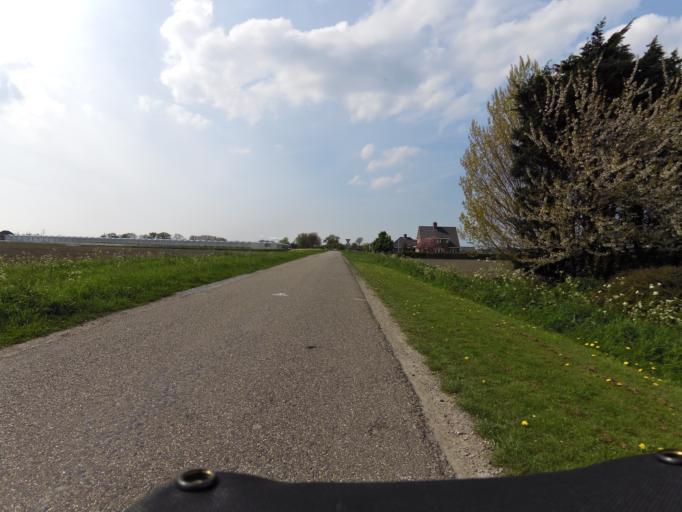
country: NL
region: South Holland
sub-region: Gemeente Brielle
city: Brielle
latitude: 51.9116
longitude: 4.1570
